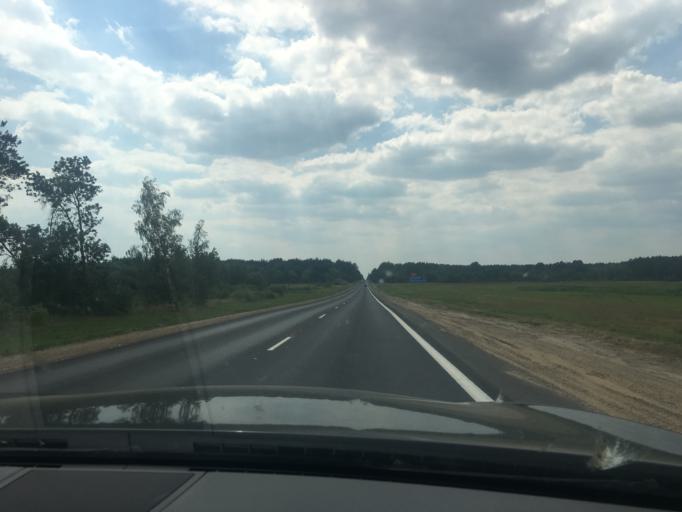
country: BY
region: Brest
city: Pruzhany
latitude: 52.5403
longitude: 24.4466
